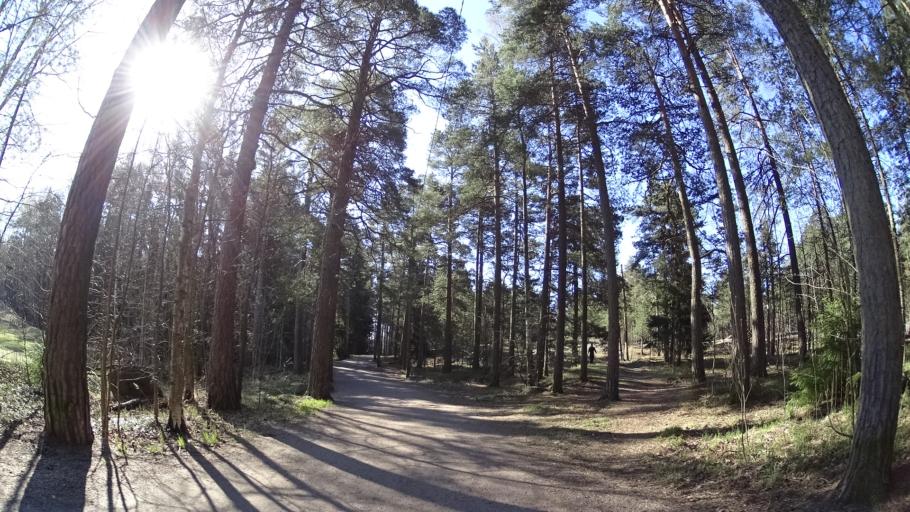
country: FI
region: Uusimaa
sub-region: Helsinki
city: Helsinki
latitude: 60.2017
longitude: 24.9099
